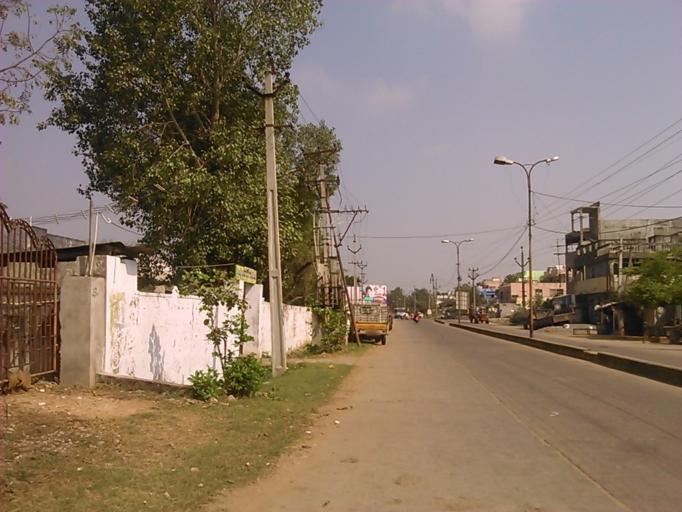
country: IN
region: Andhra Pradesh
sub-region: Guntur
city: Bhattiprolu
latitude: 16.2379
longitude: 80.6597
